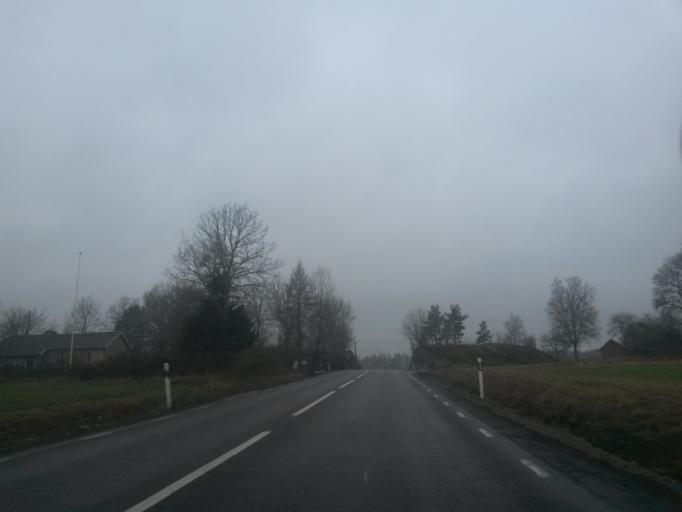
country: SE
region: Vaestra Goetaland
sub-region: Vanersborgs Kommun
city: Vargon
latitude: 58.2557
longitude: 12.4076
